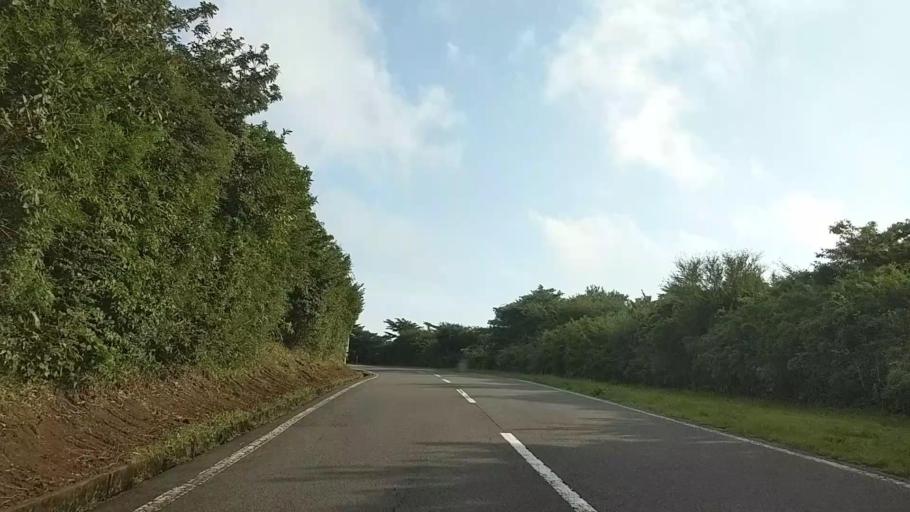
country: JP
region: Kanagawa
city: Hakone
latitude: 35.1891
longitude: 139.0019
